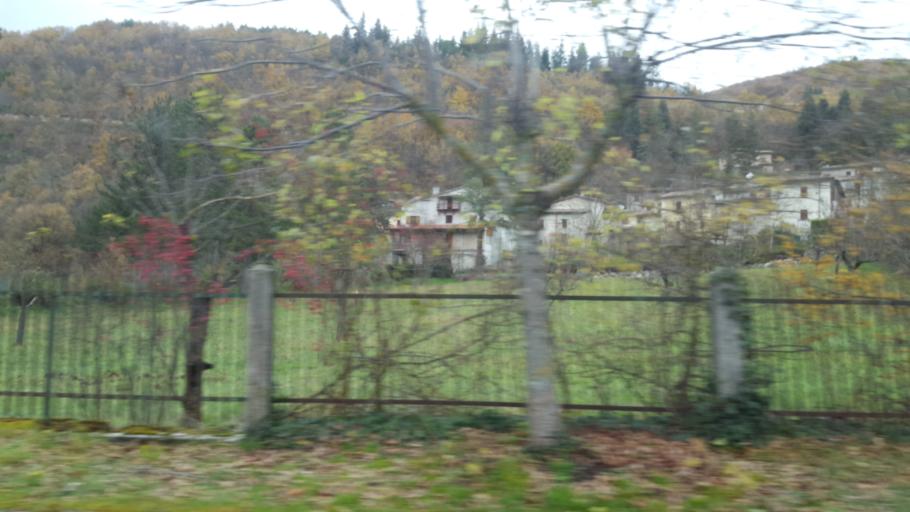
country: IT
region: The Marches
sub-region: Provincia di Macerata
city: Fluminata
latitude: 42.9434
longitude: 13.1352
